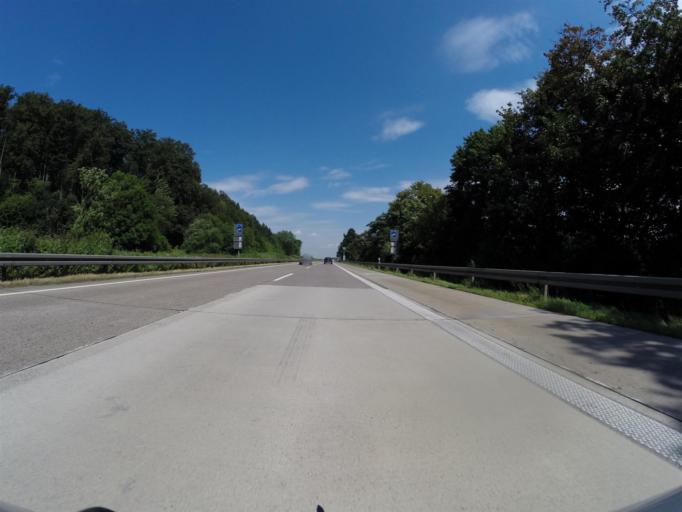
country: DE
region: Lower Saxony
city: Seesen
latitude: 51.8714
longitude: 10.1270
